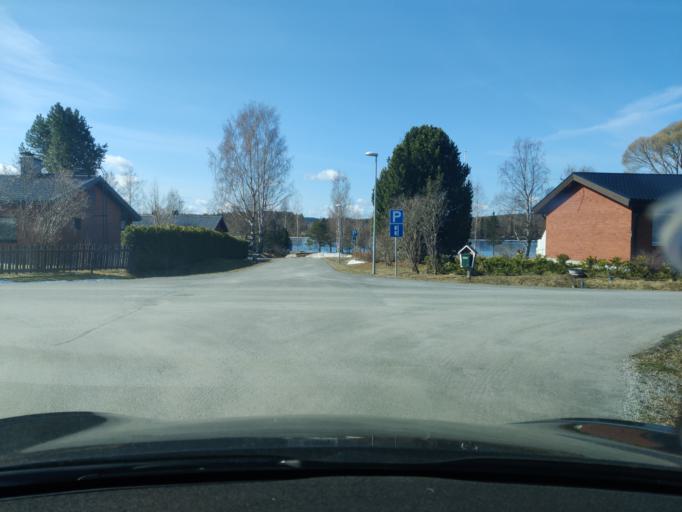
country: FI
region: Northern Savo
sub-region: Kuopio
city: Vehmersalmi
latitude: 62.7648
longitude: 28.0180
